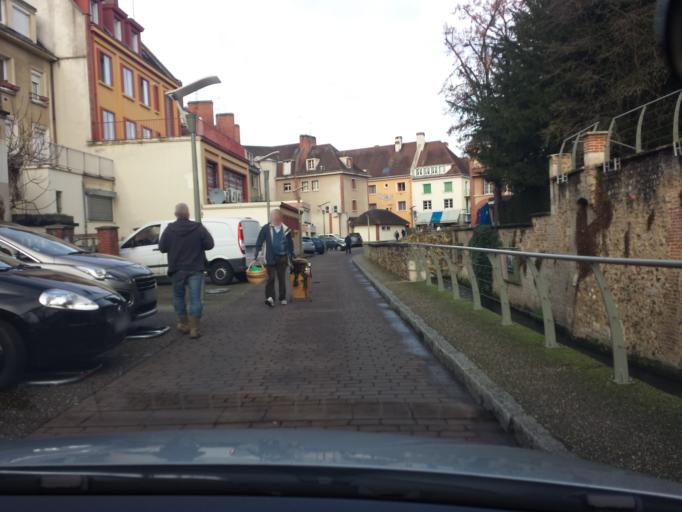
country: FR
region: Haute-Normandie
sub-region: Departement de l'Eure
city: Evreux
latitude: 49.0253
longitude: 1.1489
